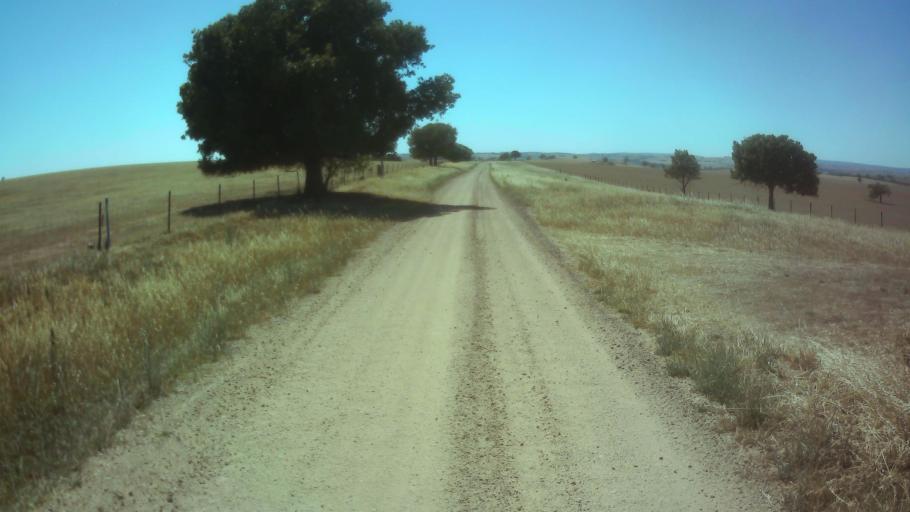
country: AU
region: New South Wales
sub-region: Weddin
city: Grenfell
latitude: -33.9660
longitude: 148.3531
